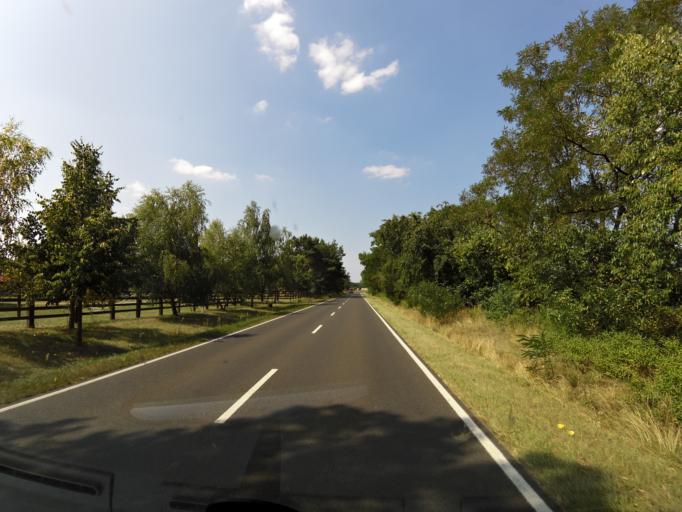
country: DE
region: Brandenburg
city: Zehdenick
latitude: 52.9476
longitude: 13.3850
